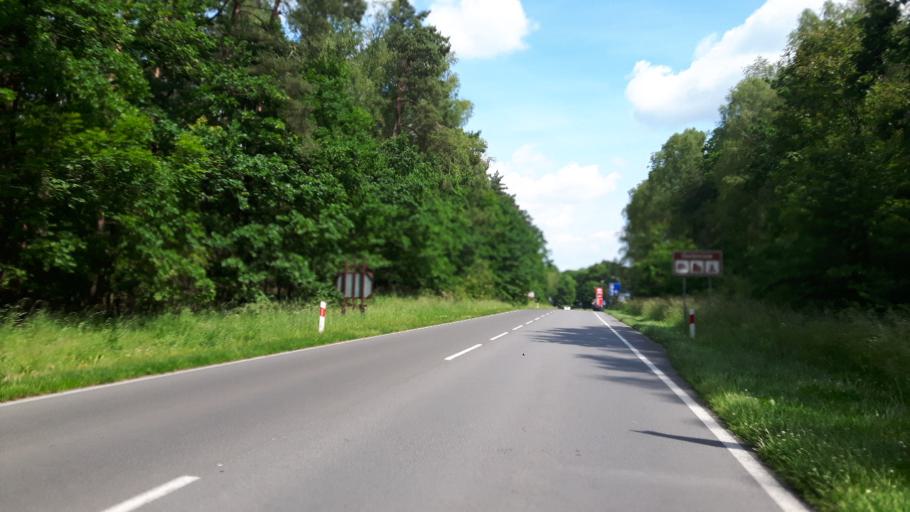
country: PL
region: West Pomeranian Voivodeship
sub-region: Powiat goleniowski
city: Goleniow
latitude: 53.5529
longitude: 14.8183
